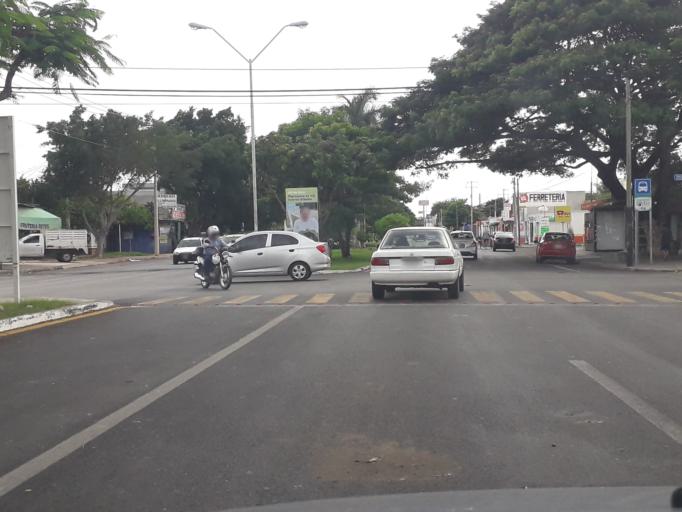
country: MX
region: Yucatan
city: Merida
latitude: 20.9648
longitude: -89.6636
